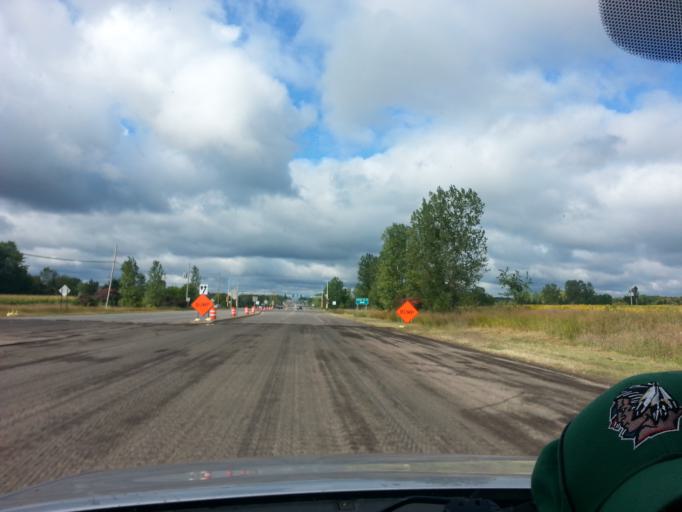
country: US
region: Minnesota
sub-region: Washington County
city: Oakdale
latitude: 44.9636
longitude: -92.9310
